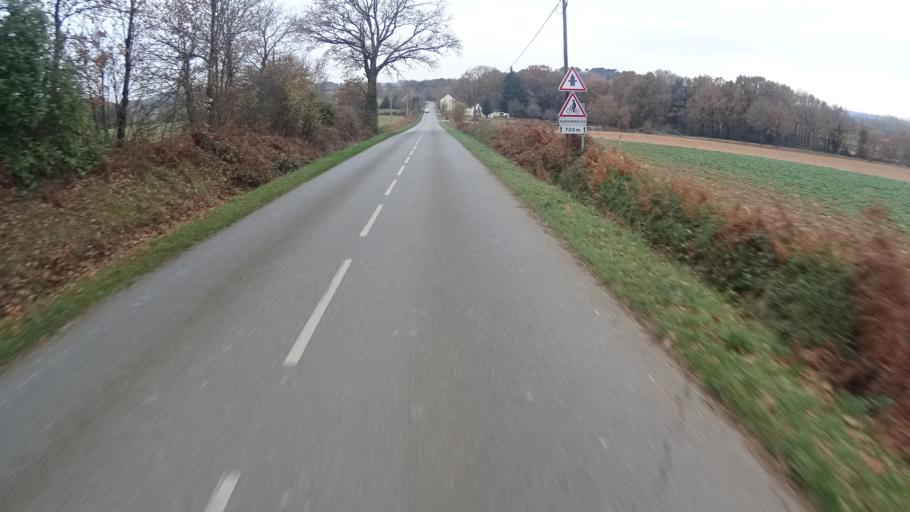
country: FR
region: Pays de la Loire
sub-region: Departement de la Loire-Atlantique
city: Avessac
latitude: 47.6668
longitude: -1.9264
